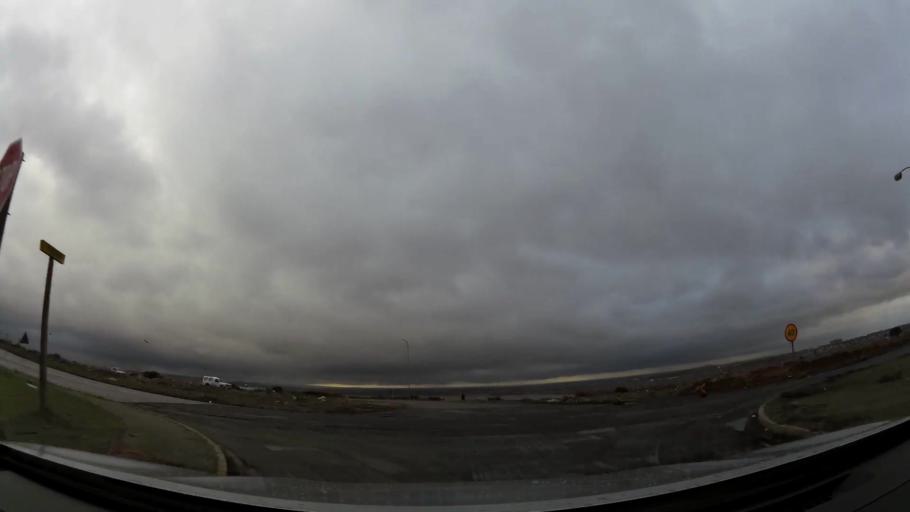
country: ZA
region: Eastern Cape
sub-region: Nelson Mandela Bay Metropolitan Municipality
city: Port Elizabeth
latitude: -33.8957
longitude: 25.5407
